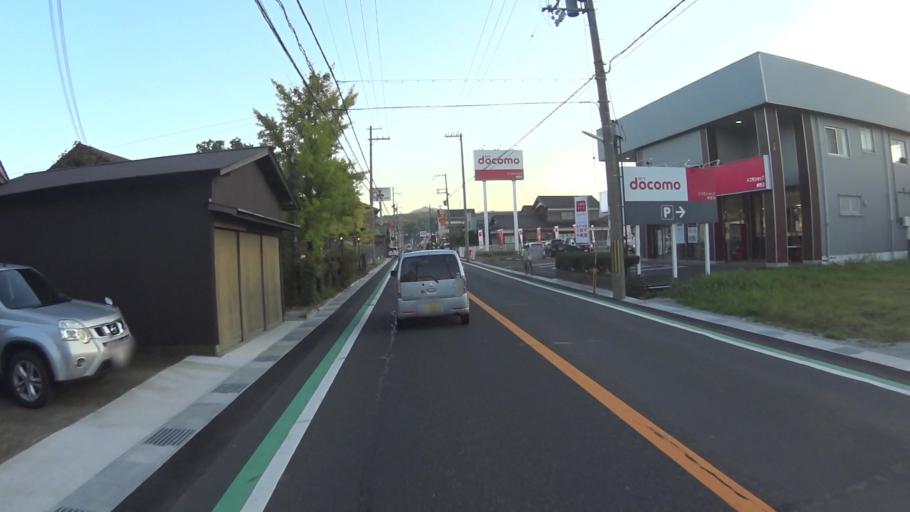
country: JP
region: Kyoto
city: Miyazu
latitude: 35.6748
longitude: 135.0281
